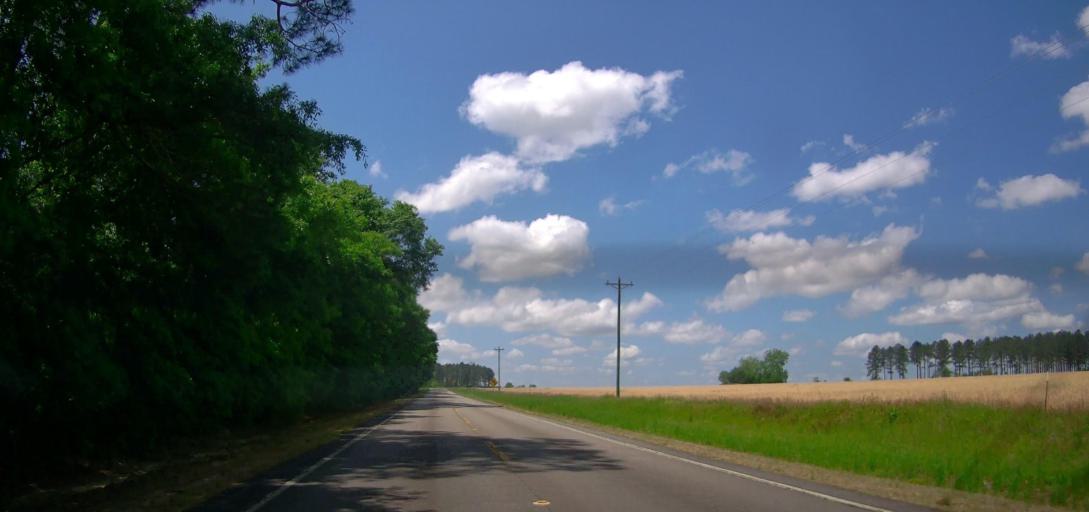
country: US
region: Georgia
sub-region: Bleckley County
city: Cochran
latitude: 32.4787
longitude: -83.2674
